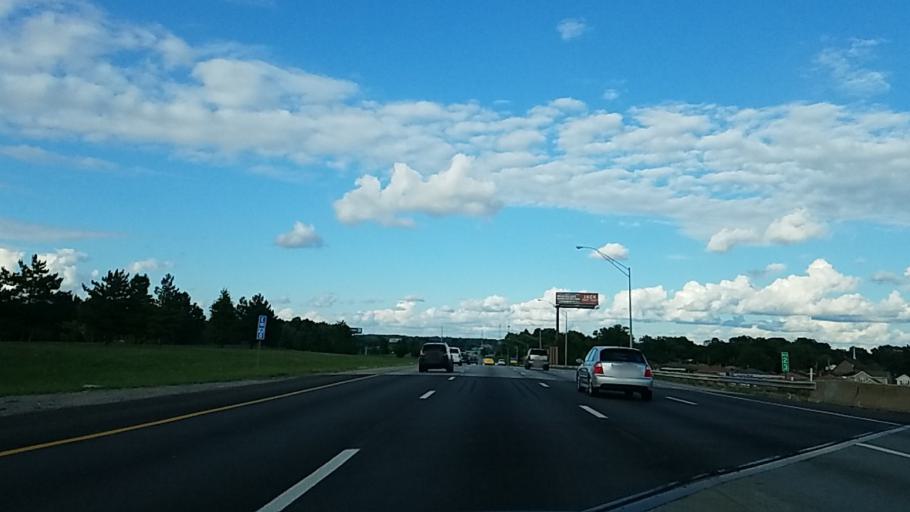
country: US
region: Ohio
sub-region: Cuyahoga County
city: Garfield Heights
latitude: 41.4173
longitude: -81.5933
